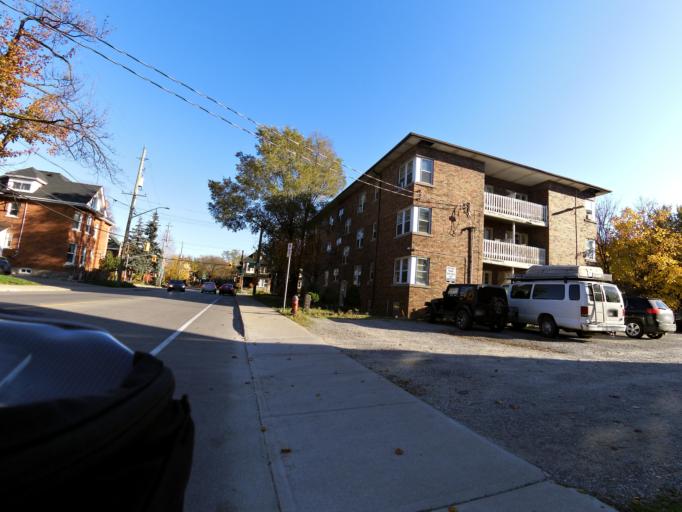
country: CA
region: Ontario
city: Hamilton
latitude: 43.2473
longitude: -79.8519
